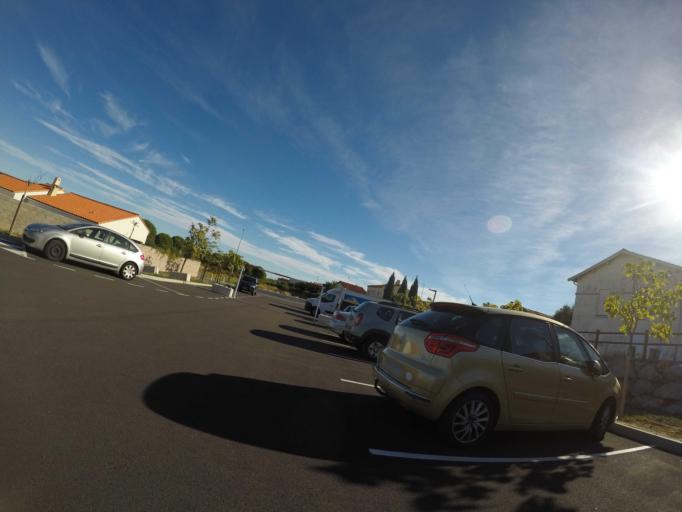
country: FR
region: Languedoc-Roussillon
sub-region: Departement des Pyrenees-Orientales
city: Villemolaque
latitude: 42.5800
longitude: 2.8122
